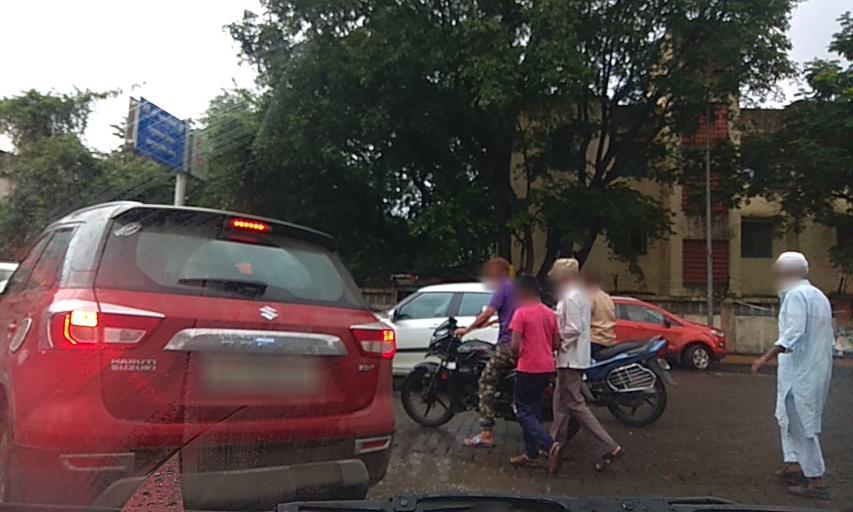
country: IN
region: Maharashtra
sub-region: Pune Division
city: Khadki
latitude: 18.5494
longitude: 73.8548
